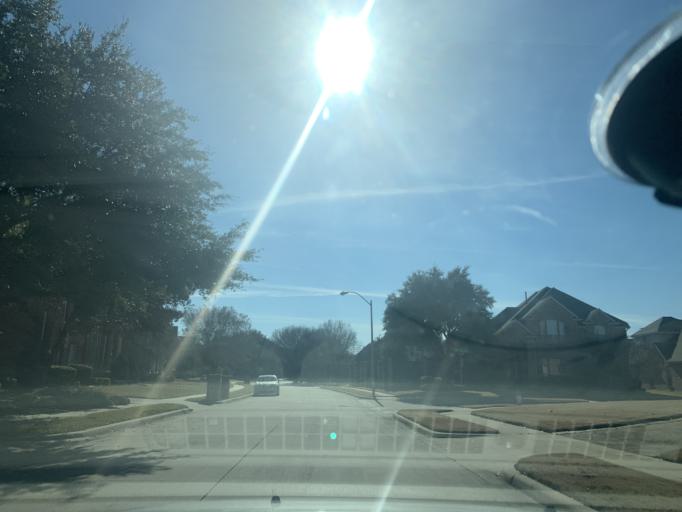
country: US
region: Texas
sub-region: Denton County
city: The Colony
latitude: 33.0537
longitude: -96.8216
